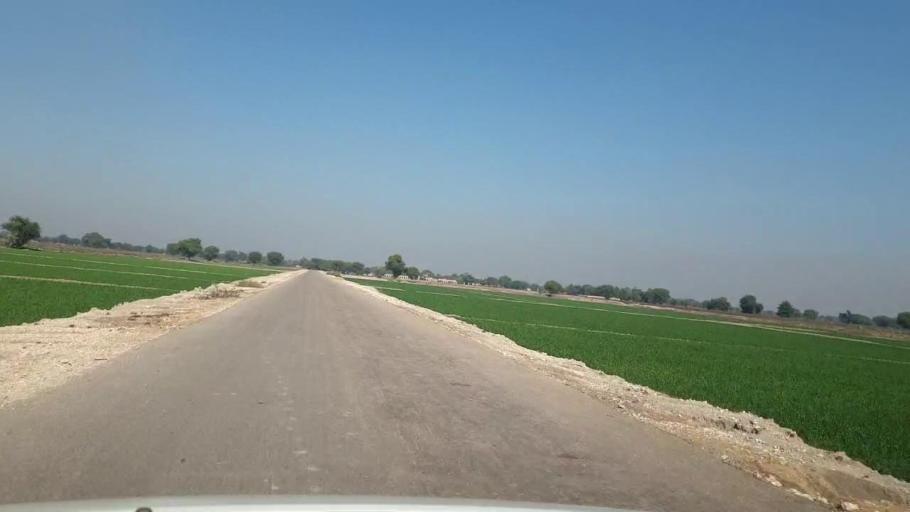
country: PK
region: Sindh
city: Johi
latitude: 26.6594
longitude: 67.7058
